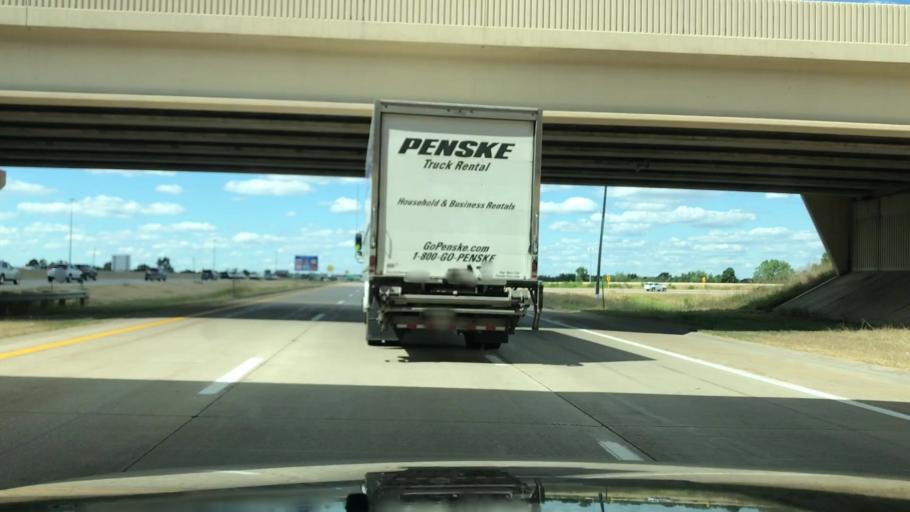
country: US
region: Michigan
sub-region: Kent County
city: Cutlerville
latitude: 42.8490
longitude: -85.6781
